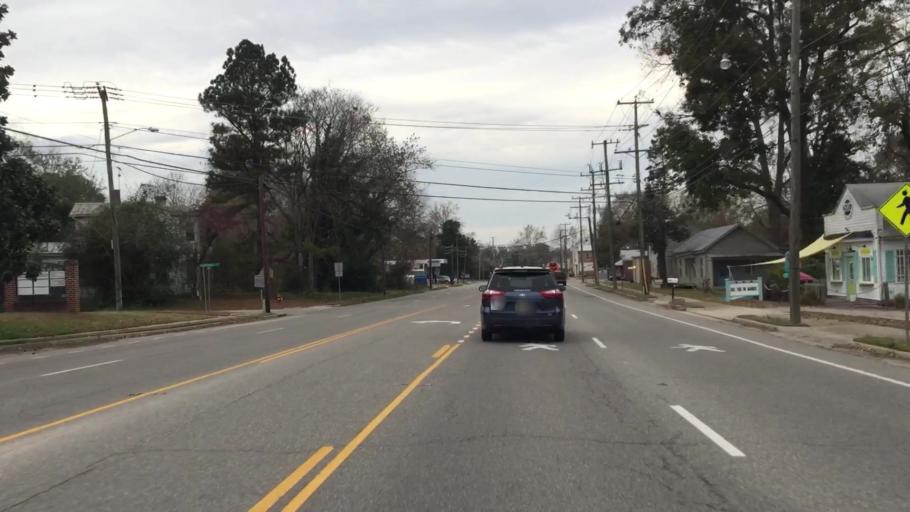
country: US
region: Virginia
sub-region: James City County
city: Williamsburg
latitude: 37.3789
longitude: -76.8026
